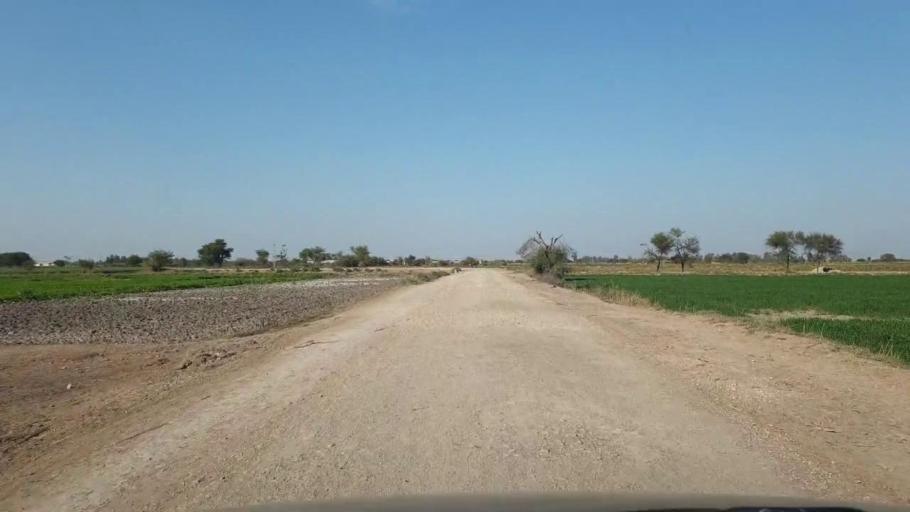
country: PK
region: Sindh
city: Shahpur Chakar
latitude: 26.1676
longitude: 68.6819
